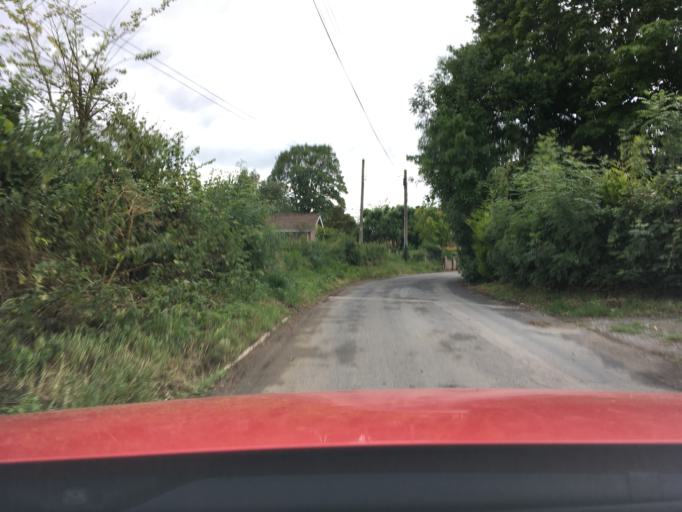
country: GB
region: England
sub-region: Gloucestershire
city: Cinderford
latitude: 51.7995
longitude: -2.4218
